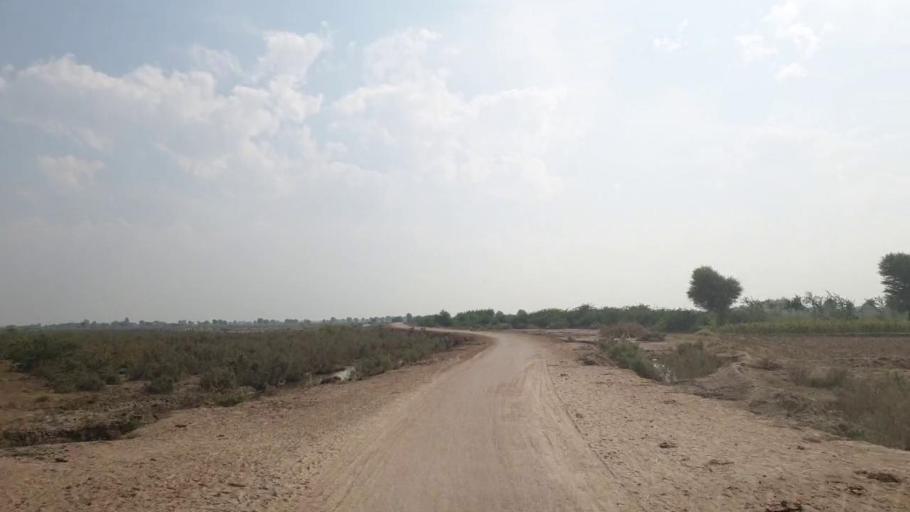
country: PK
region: Sindh
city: Rajo Khanani
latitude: 24.9677
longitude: 69.0098
